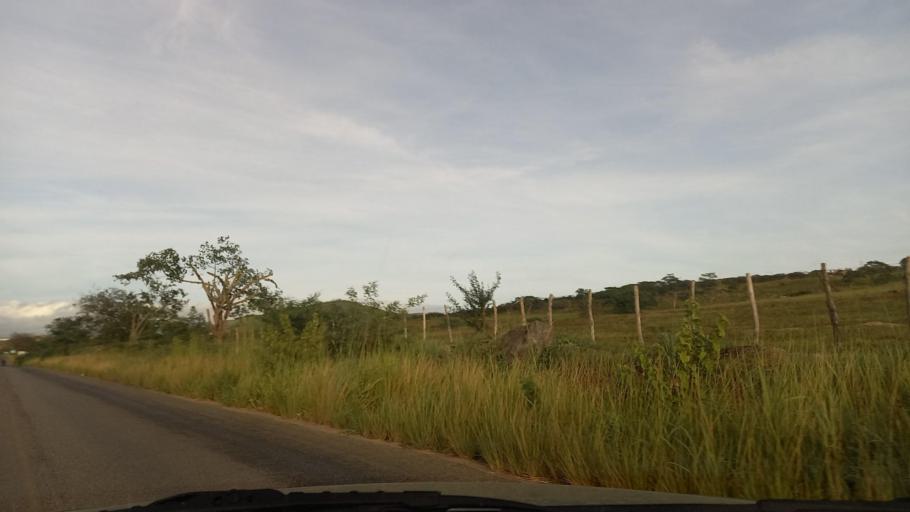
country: BR
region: Pernambuco
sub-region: Bezerros
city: Bezerros
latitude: -8.2135
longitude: -35.7417
